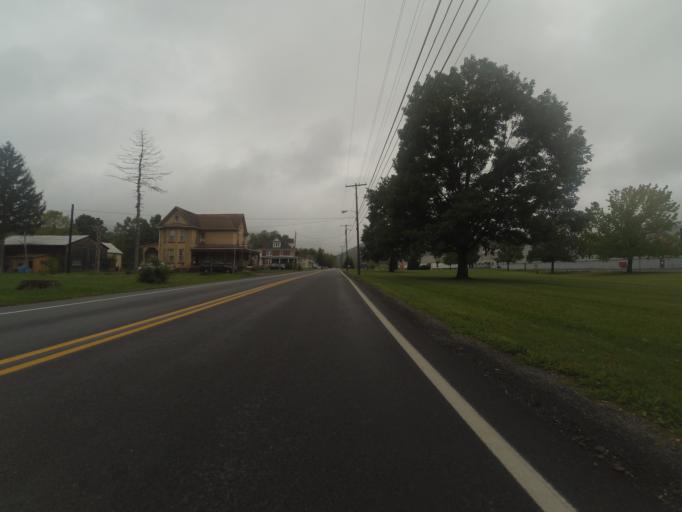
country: US
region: Pennsylvania
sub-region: Huntingdon County
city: McConnellstown
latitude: 40.5620
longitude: -78.1097
